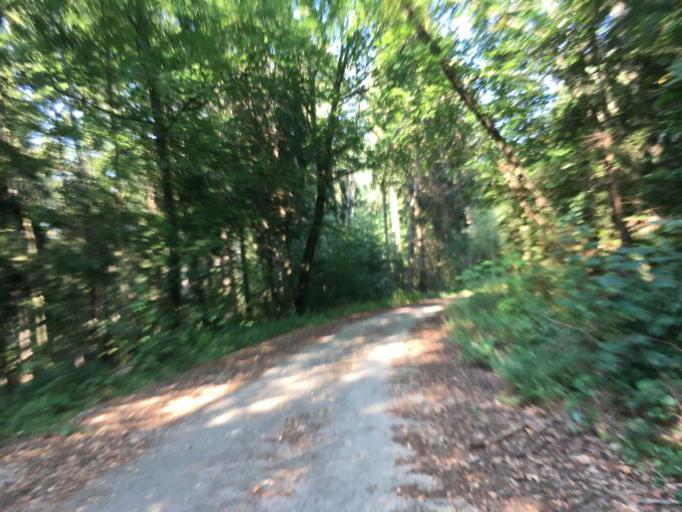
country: DE
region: Baden-Wuerttemberg
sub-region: Tuebingen Region
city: Kusterdingen
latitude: 48.5045
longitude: 9.0877
